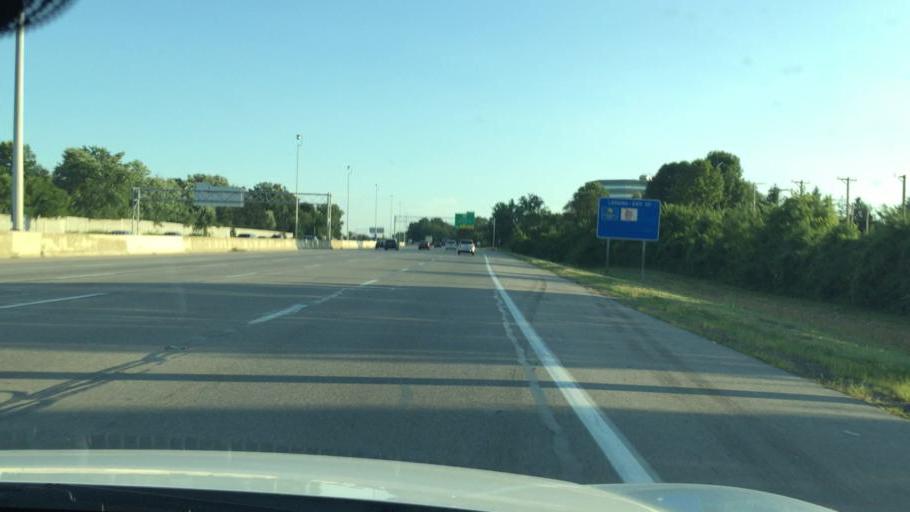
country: US
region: Ohio
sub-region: Franklin County
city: Worthington
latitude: 40.1049
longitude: -82.9820
